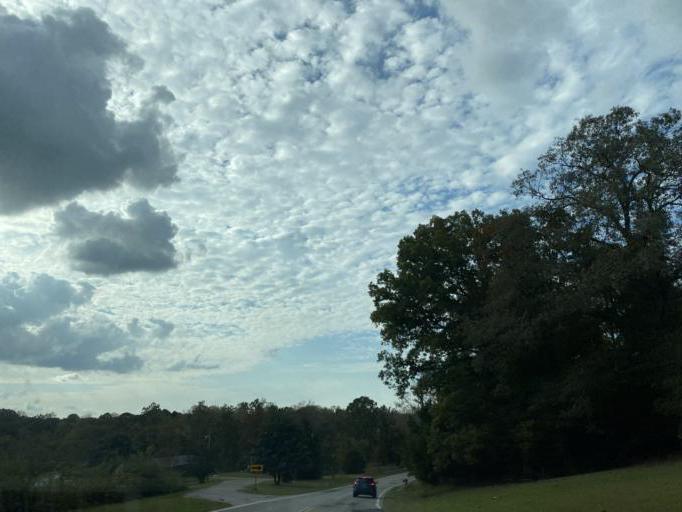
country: US
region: South Carolina
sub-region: Cherokee County
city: Gaffney
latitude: 35.0715
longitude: -81.7217
